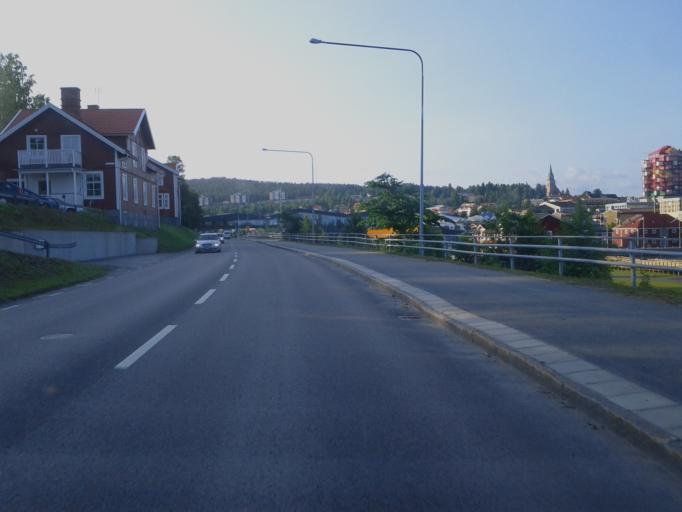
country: SE
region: Vaesternorrland
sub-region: OErnskoeldsviks Kommun
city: Ornskoldsvik
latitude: 63.2854
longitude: 18.7079
